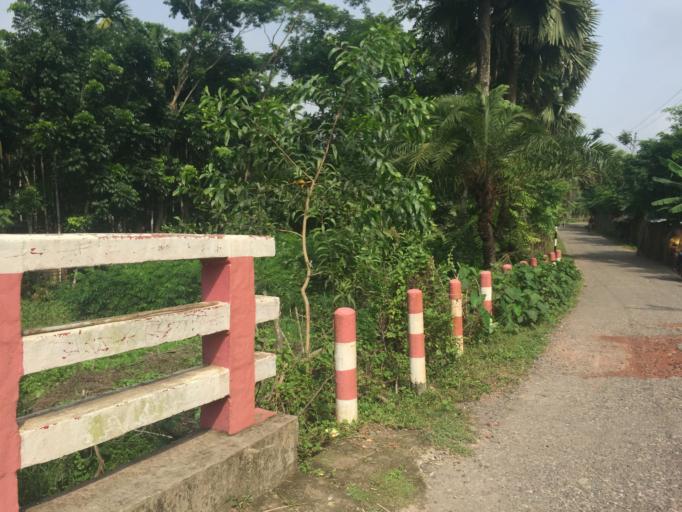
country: BD
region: Barisal
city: Mathba
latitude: 22.2617
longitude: 89.9109
